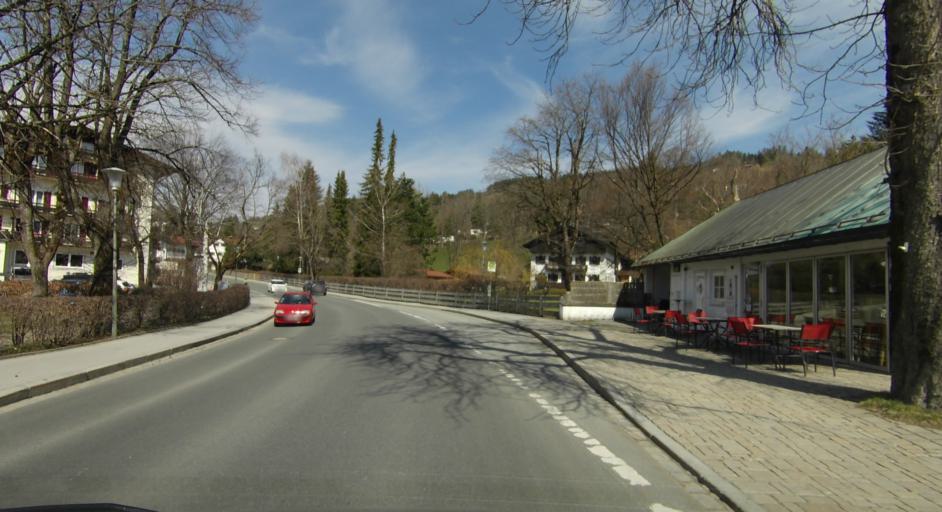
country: DE
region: Bavaria
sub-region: Upper Bavaria
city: Schliersee
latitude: 47.7311
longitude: 11.8686
